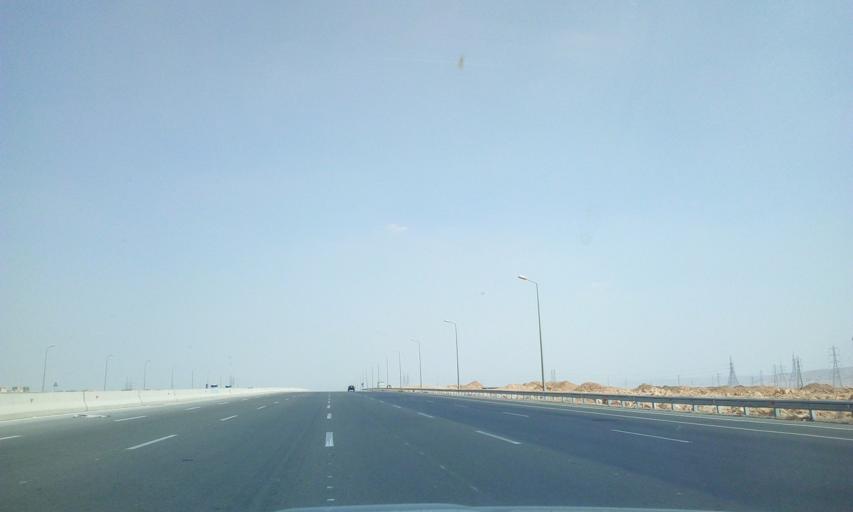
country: EG
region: Muhafazat al Qahirah
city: Halwan
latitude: 29.9226
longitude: 31.6153
